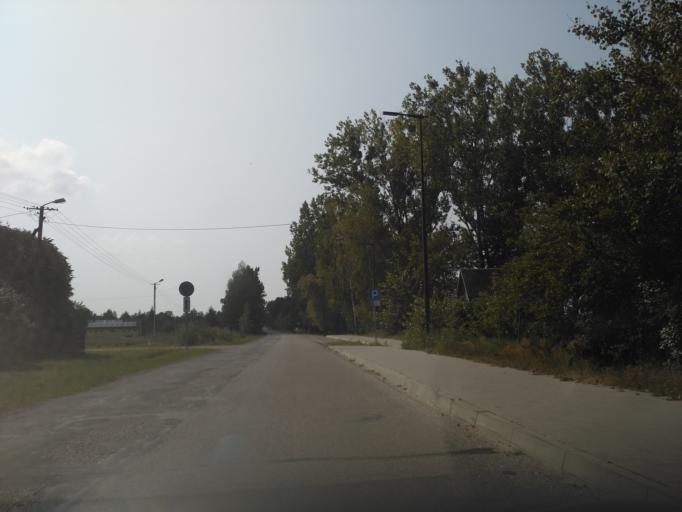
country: PL
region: Lublin Voivodeship
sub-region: Powiat wlodawski
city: Urszulin
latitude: 51.3716
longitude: 23.1529
